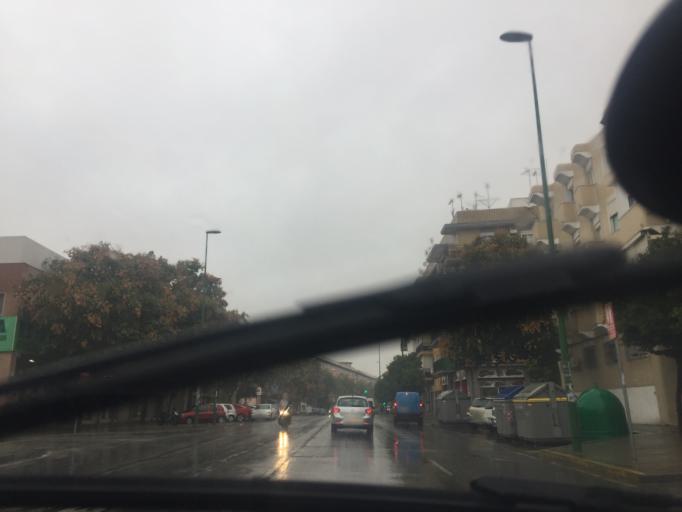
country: ES
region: Andalusia
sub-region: Provincia de Sevilla
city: Sevilla
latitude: 37.3685
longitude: -5.9562
